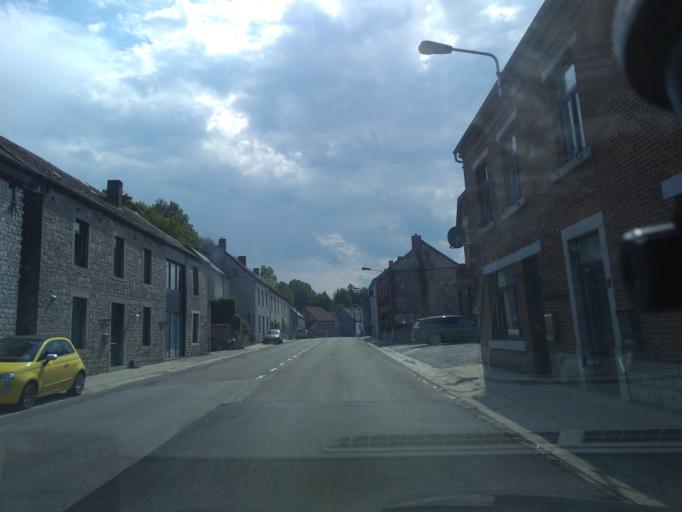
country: BE
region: Wallonia
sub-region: Province de Namur
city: Dinant
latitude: 50.2044
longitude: 4.8957
